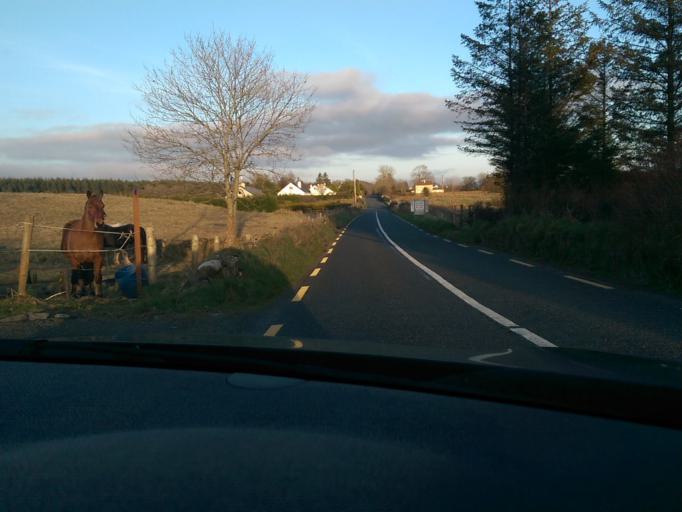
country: IE
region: Connaught
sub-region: Sligo
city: Tobercurry
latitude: 54.0514
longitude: -8.7071
